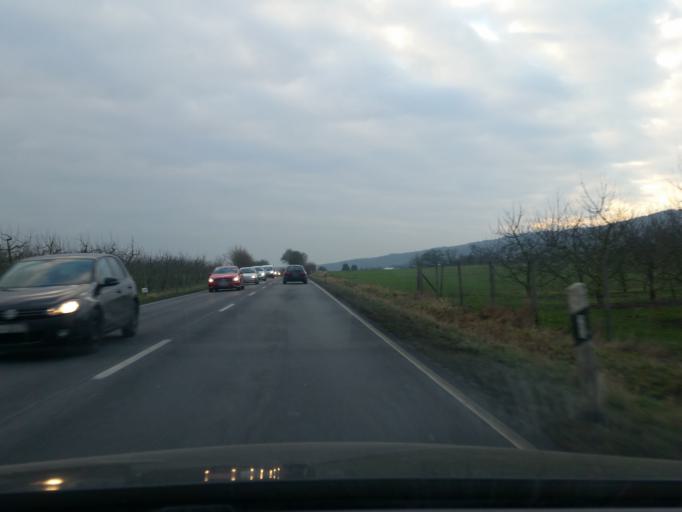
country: DE
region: Hesse
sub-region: Regierungsbezirk Darmstadt
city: Rosbach vor der Hohe
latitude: 50.3145
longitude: 8.7062
